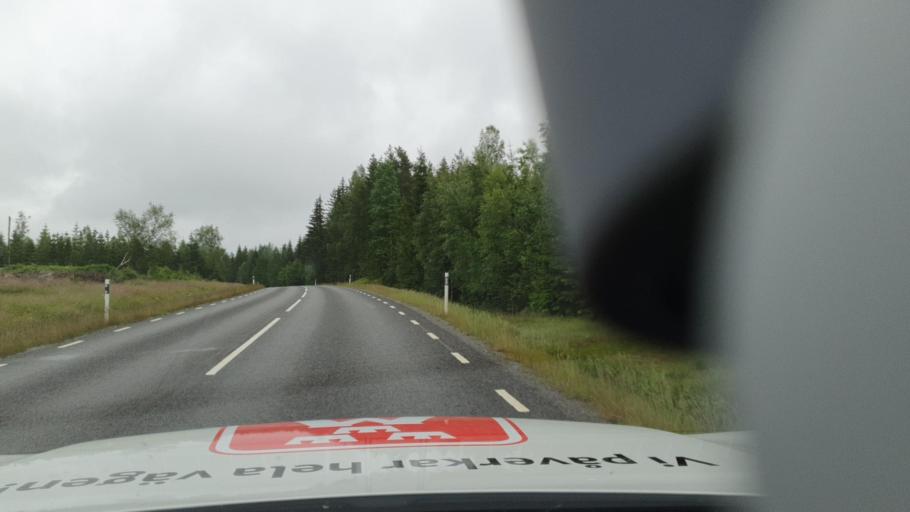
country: SE
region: OErebro
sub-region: Degerfors Kommun
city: Degerfors
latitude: 59.2219
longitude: 14.3456
